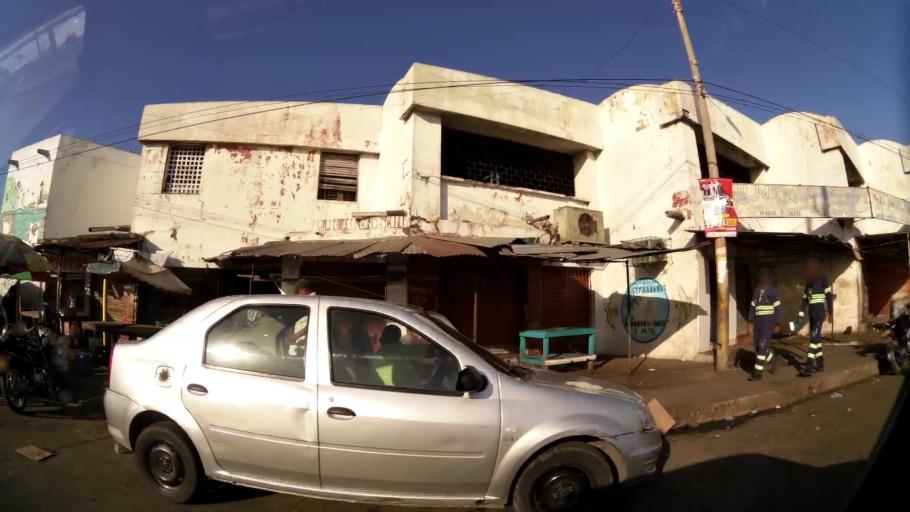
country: CO
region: Bolivar
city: Cartagena
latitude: 10.4118
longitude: -75.5255
